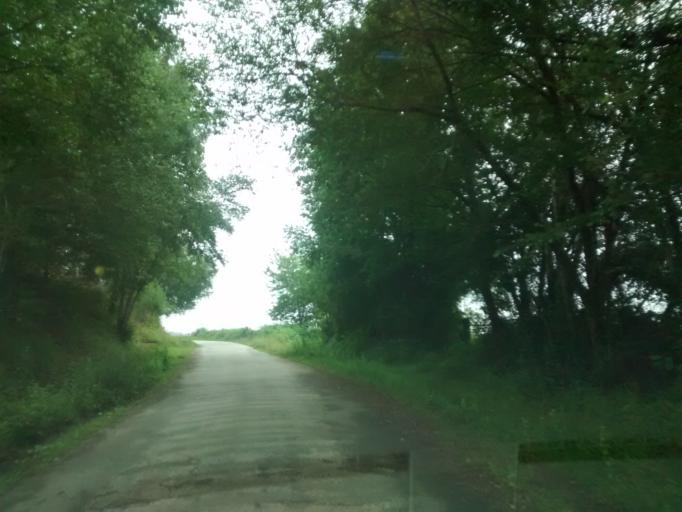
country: ES
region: Galicia
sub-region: Provincia de Ourense
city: Castro Caldelas
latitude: 42.4032
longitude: -7.3976
